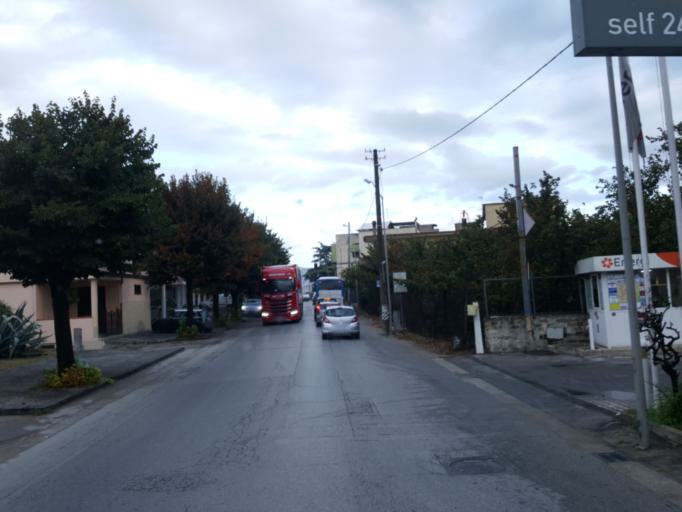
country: IT
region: Campania
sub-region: Provincia di Napoli
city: Palma Campania
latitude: 40.8788
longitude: 14.5508
